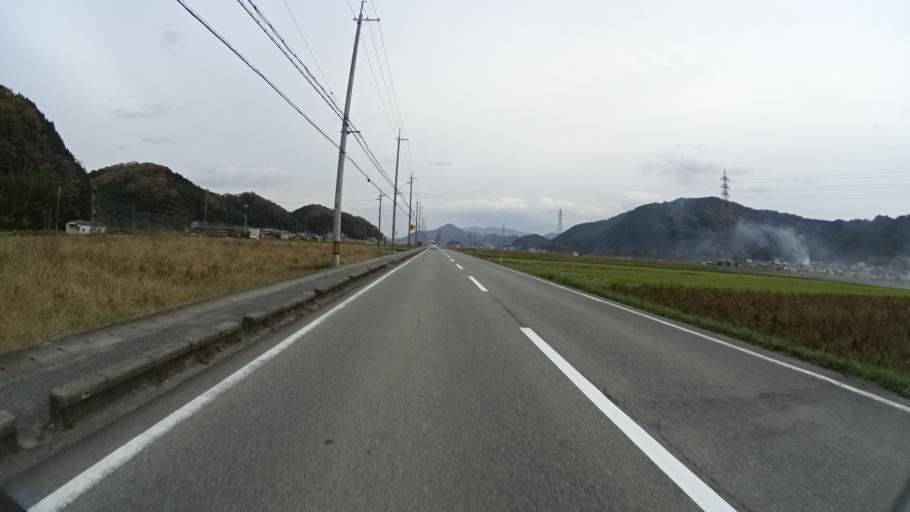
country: JP
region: Hyogo
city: Sasayama
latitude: 35.0636
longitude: 135.1975
